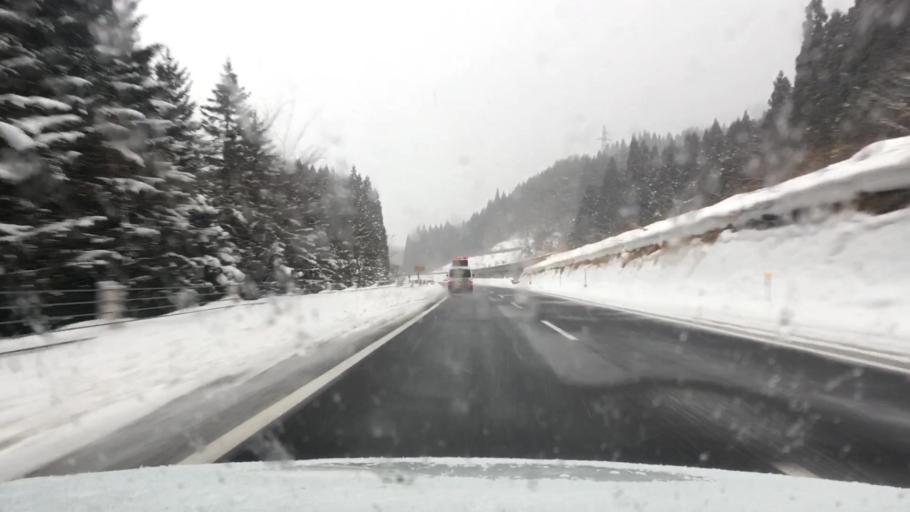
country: JP
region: Akita
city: Hanawa
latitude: 40.1440
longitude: 140.8084
